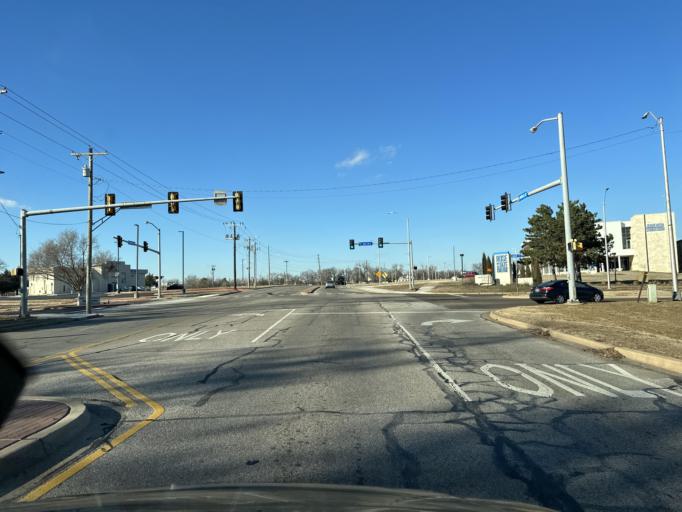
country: US
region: Oklahoma
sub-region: Oklahoma County
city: Midwest City
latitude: 35.4422
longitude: -97.4157
